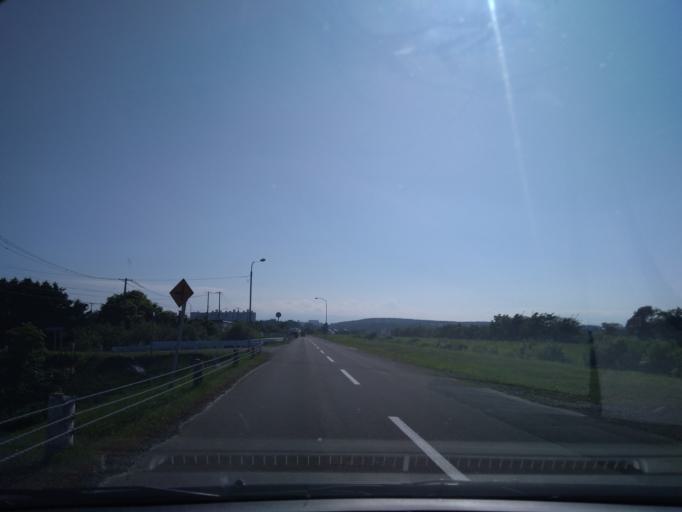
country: JP
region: Hokkaido
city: Kitahiroshima
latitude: 42.9913
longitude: 141.5784
